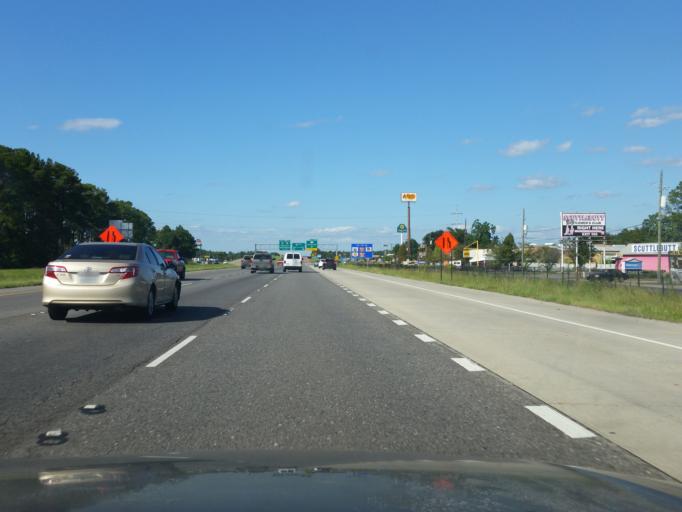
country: US
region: Louisiana
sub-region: Saint Tammany Parish
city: Slidell
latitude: 30.2786
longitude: -89.7517
